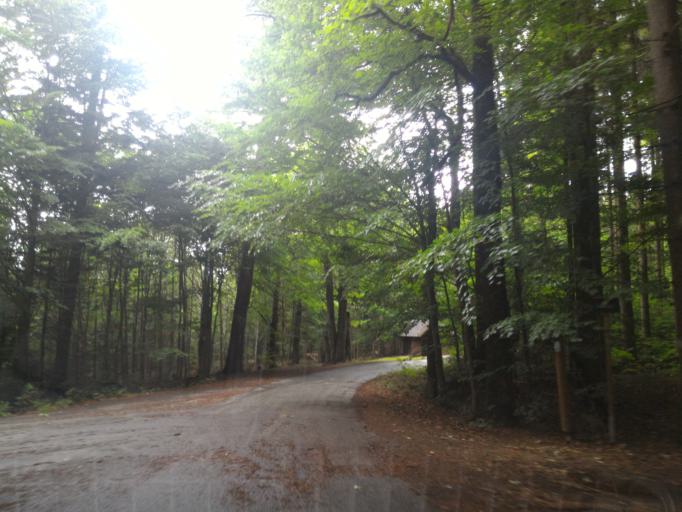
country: CZ
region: Vysocina
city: Batelov
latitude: 49.2526
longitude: 15.4224
